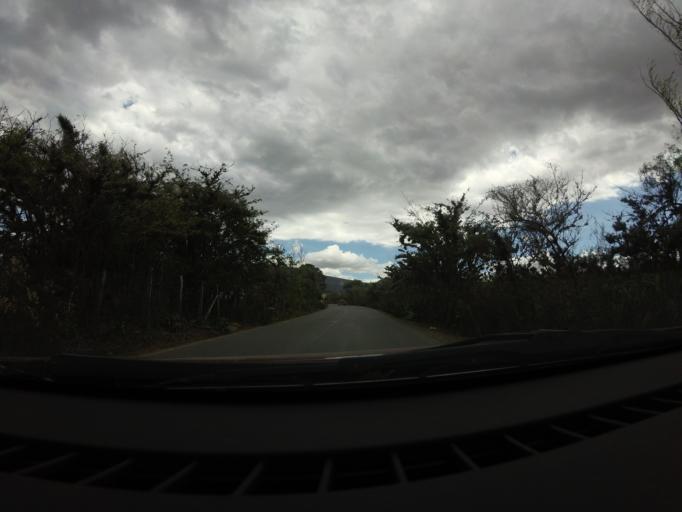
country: CO
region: Boyaca
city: Villa de Leiva
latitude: 5.6409
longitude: -73.5643
